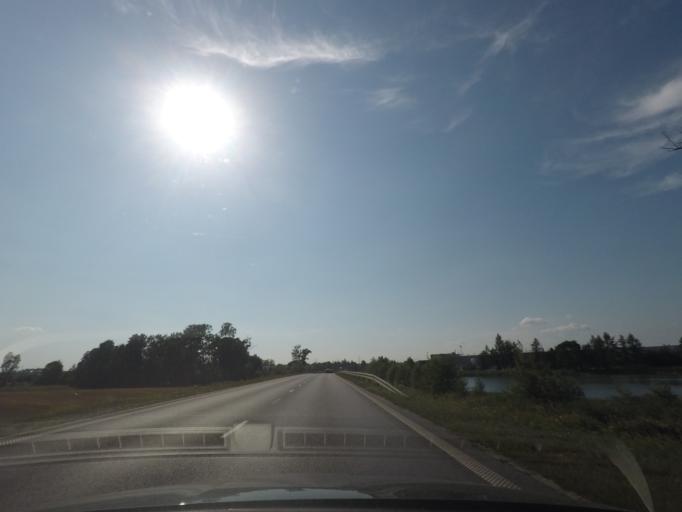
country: PL
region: Silesian Voivodeship
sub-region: Zory
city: Zory
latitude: 50.0590
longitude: 18.6782
